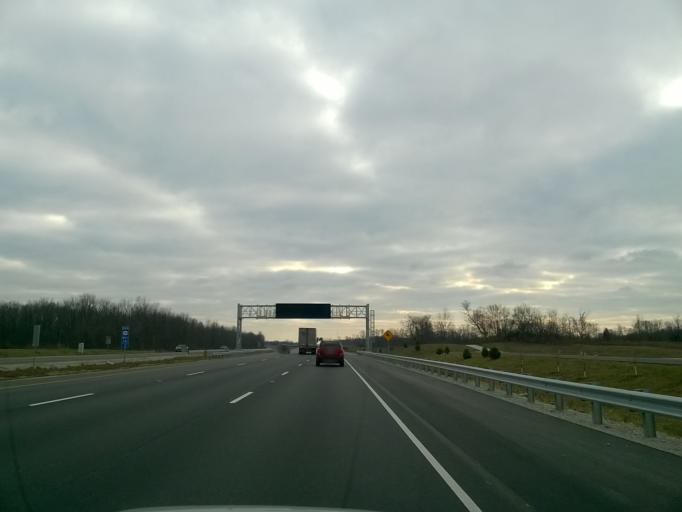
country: US
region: Indiana
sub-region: Hamilton County
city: Westfield
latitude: 40.0288
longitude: -86.1344
